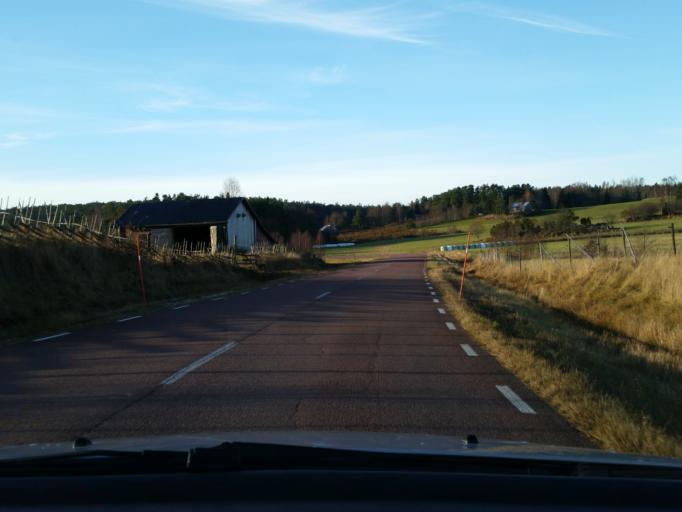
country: AX
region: Alands landsbygd
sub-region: Sund
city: Sund
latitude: 60.2990
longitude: 20.1322
